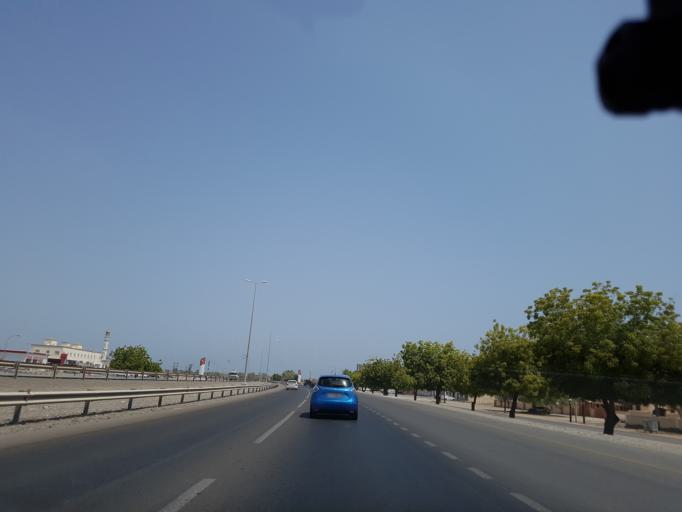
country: OM
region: Al Batinah
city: Saham
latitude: 24.1911
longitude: 56.8590
